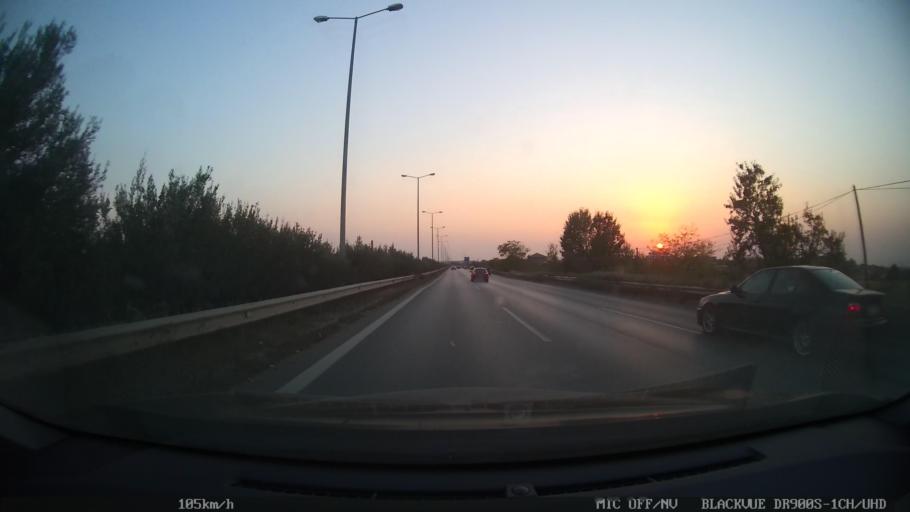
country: GR
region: Central Macedonia
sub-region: Nomos Thessalonikis
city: Pylaia
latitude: 40.5872
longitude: 22.9848
